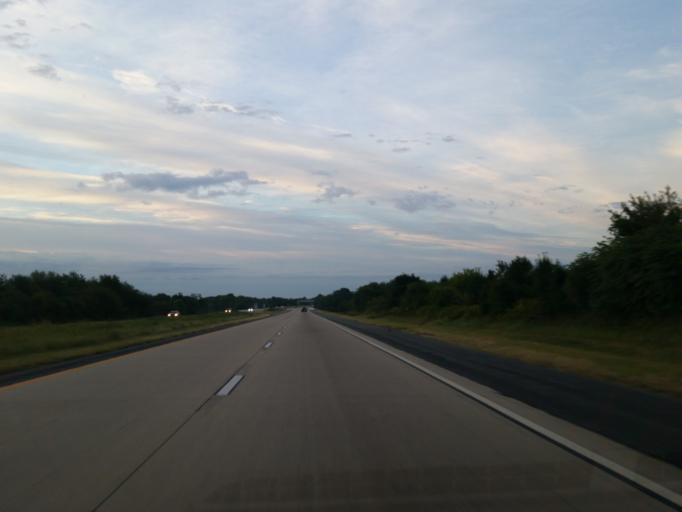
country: US
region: Delaware
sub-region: Kent County
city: Smyrna
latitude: 39.3146
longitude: -75.6009
